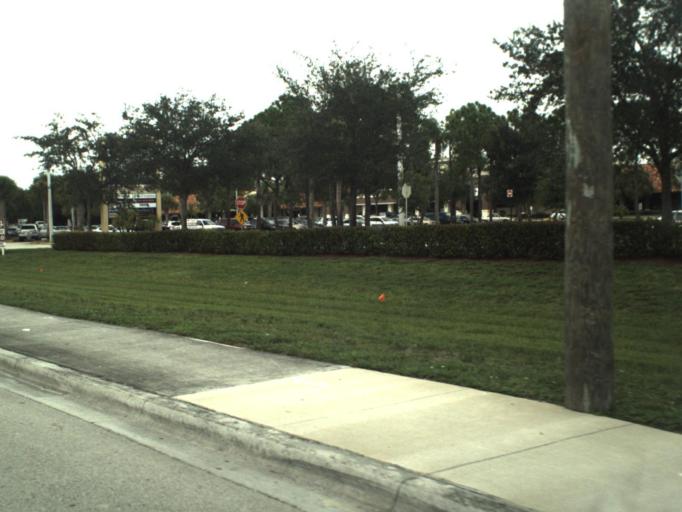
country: US
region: Florida
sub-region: Palm Beach County
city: Greenacres City
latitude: 26.6176
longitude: -80.1673
